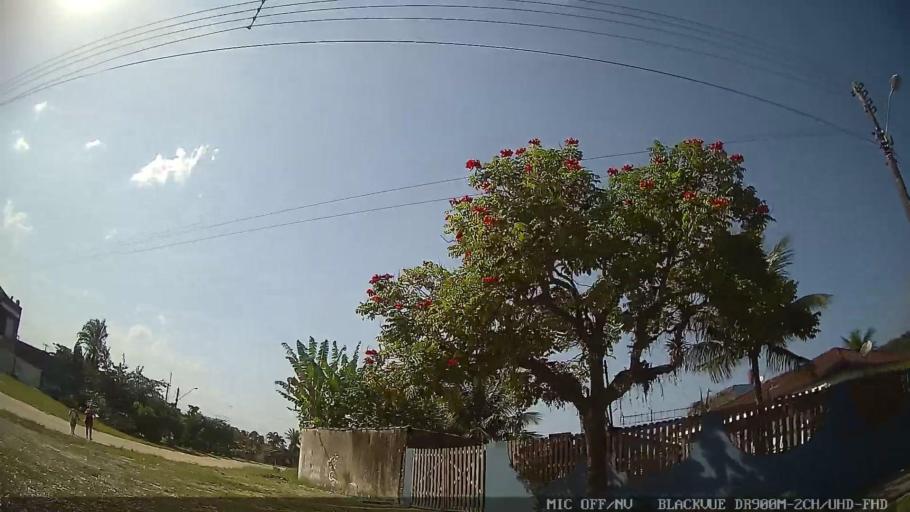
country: BR
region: Sao Paulo
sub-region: Guaruja
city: Guaruja
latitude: -23.9785
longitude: -46.1999
